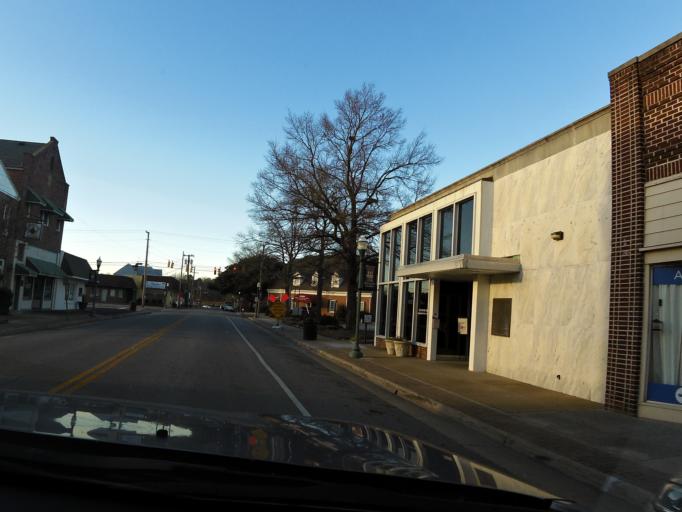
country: US
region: Virginia
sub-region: City of Franklin
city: Franklin
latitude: 36.6785
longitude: -76.9233
